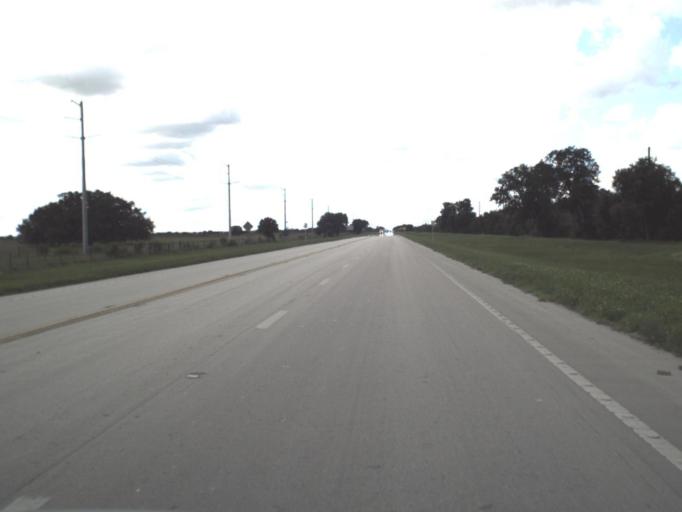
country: US
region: Florida
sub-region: DeSoto County
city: Southeast Arcadia
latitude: 27.2096
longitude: -81.6357
